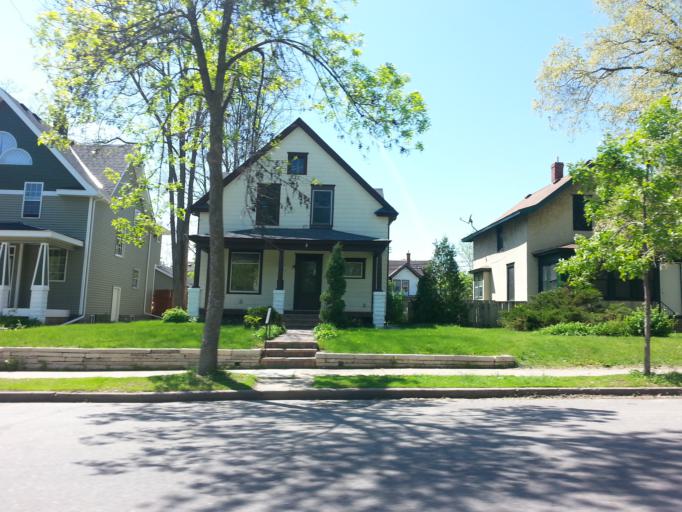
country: US
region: Minnesota
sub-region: Hennepin County
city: Minneapolis
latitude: 44.9372
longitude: -93.2625
